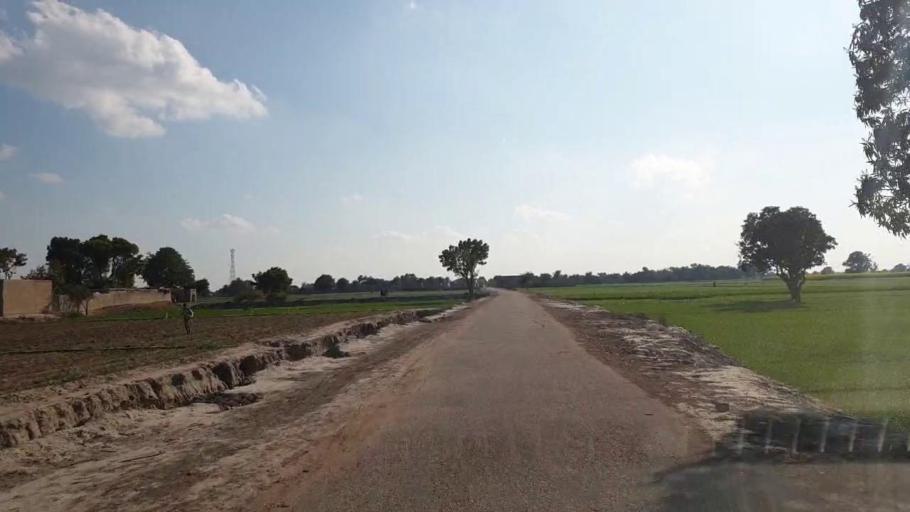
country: PK
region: Sindh
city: Shahpur Chakar
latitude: 26.1087
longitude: 68.5645
